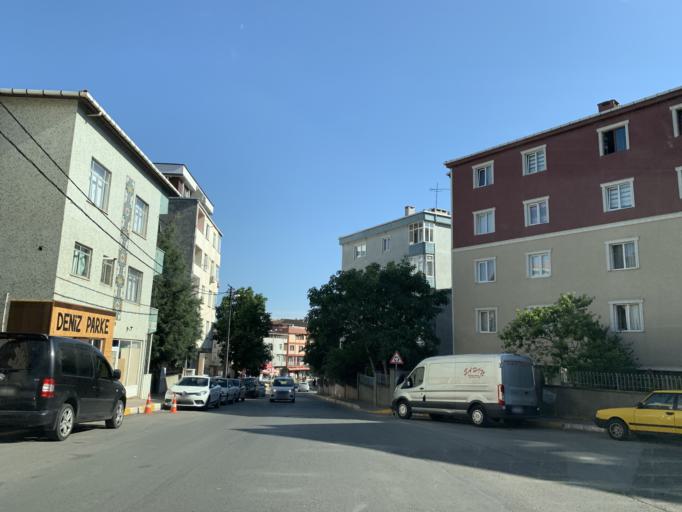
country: TR
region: Istanbul
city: Pendik
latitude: 40.8840
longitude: 29.2683
